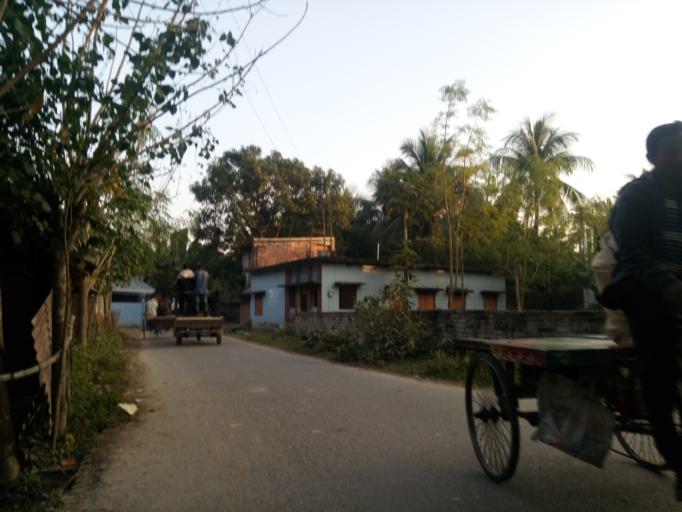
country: BD
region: Khulna
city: Kaliganj
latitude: 23.3552
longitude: 88.9202
